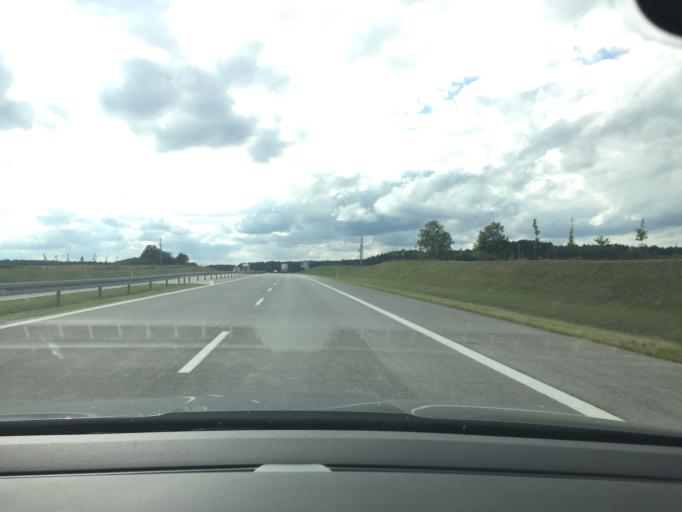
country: PL
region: Lubusz
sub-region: Powiat sulecinski
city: Torzym
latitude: 52.3240
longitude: 15.1747
